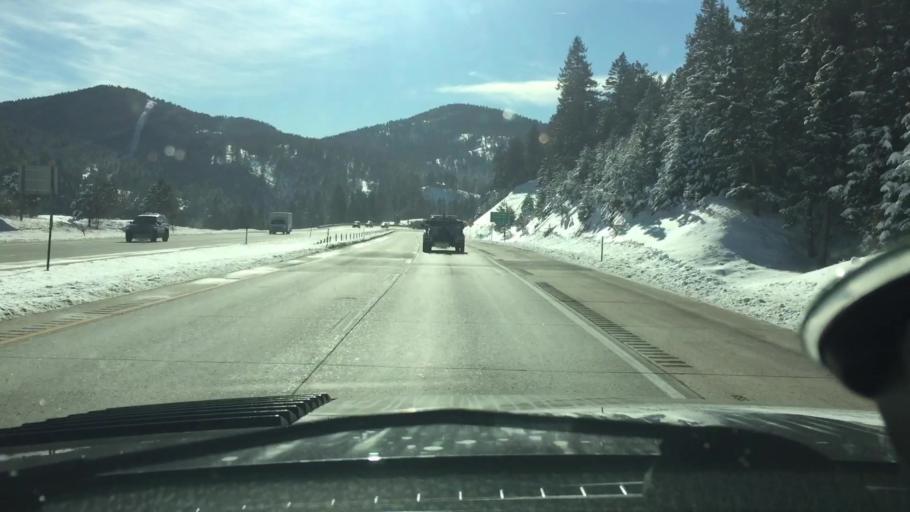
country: US
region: Colorado
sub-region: Jefferson County
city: Indian Hills
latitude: 39.5974
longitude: -105.2252
